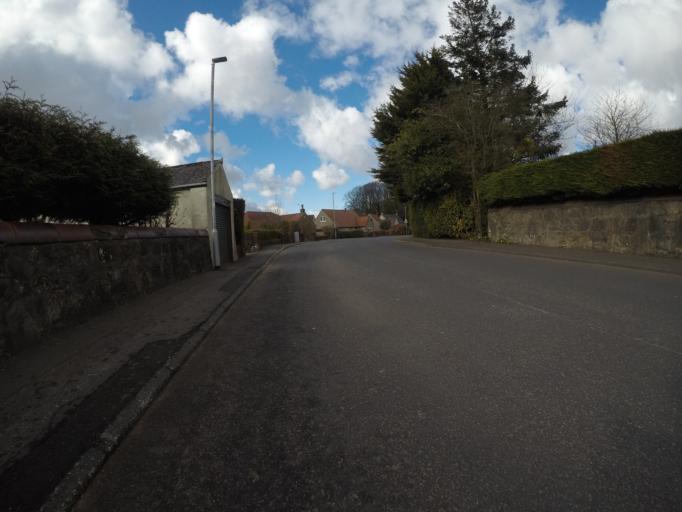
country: GB
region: Scotland
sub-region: North Ayrshire
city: Beith
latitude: 55.7467
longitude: -4.6300
